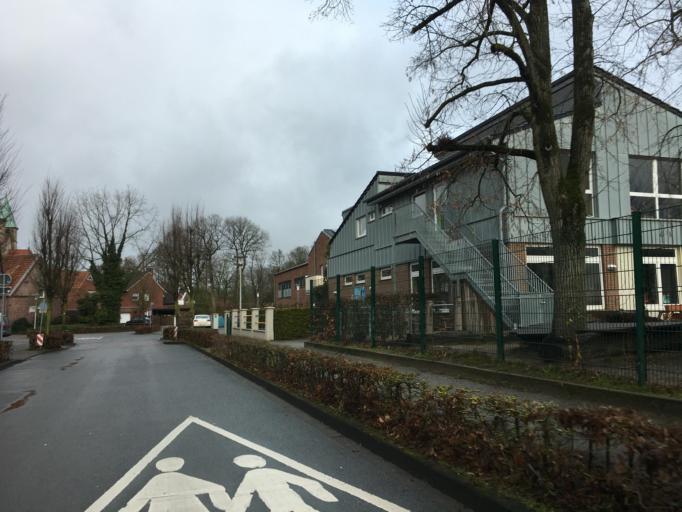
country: DE
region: North Rhine-Westphalia
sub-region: Regierungsbezirk Munster
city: Senden
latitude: 51.9171
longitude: 7.4789
